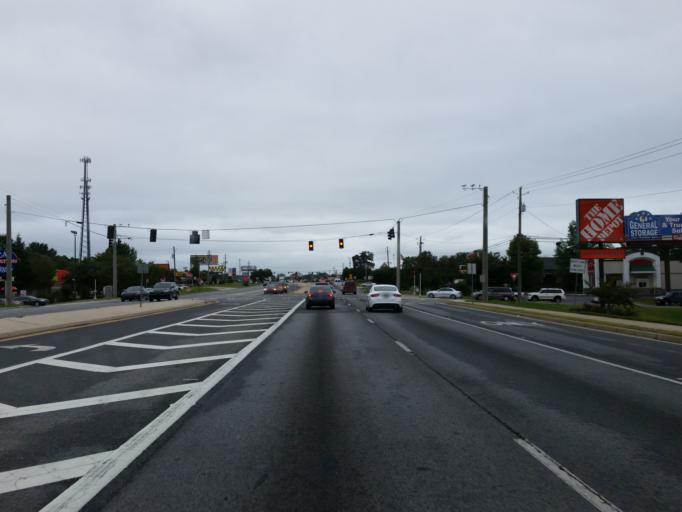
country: US
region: Georgia
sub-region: Clayton County
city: Bonanza
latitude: 33.4528
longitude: -84.3263
